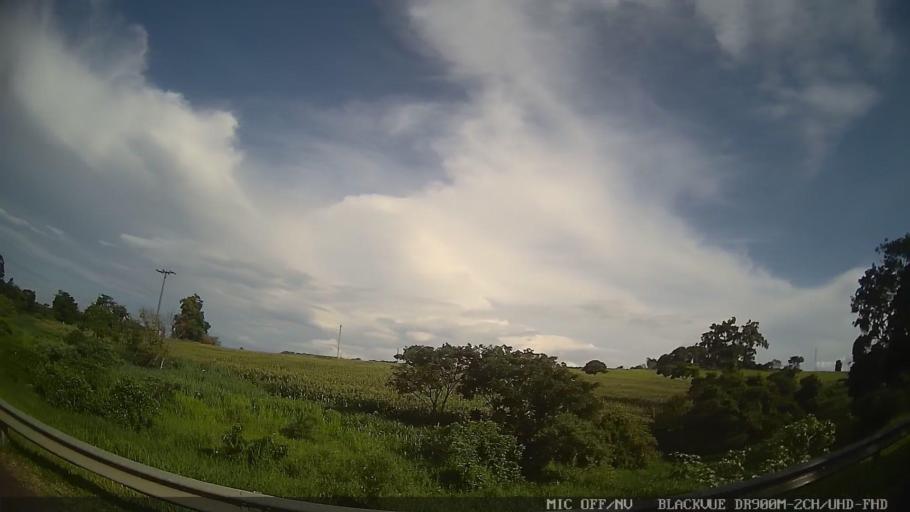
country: BR
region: Sao Paulo
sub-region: Tiete
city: Tiete
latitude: -23.1069
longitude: -47.7612
